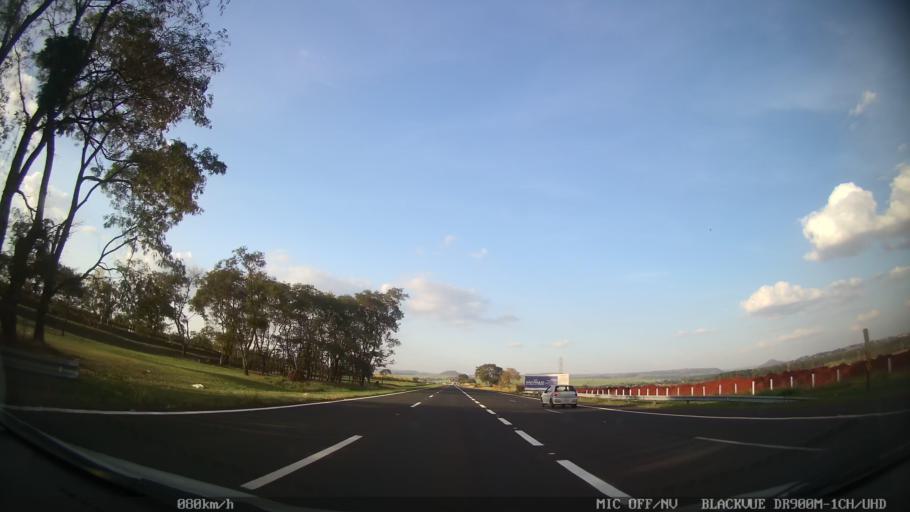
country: BR
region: Sao Paulo
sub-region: Ribeirao Preto
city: Ribeirao Preto
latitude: -21.1121
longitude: -47.7771
